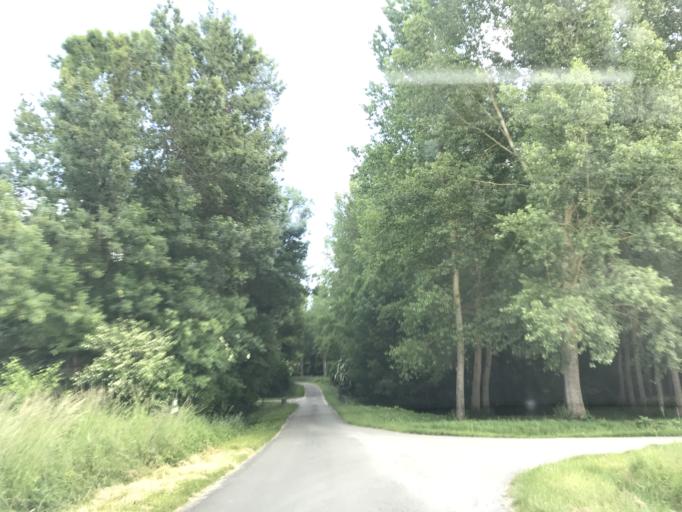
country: FR
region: Aquitaine
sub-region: Departement de la Dordogne
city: Saint-Aulaye
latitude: 45.2650
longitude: 0.1236
